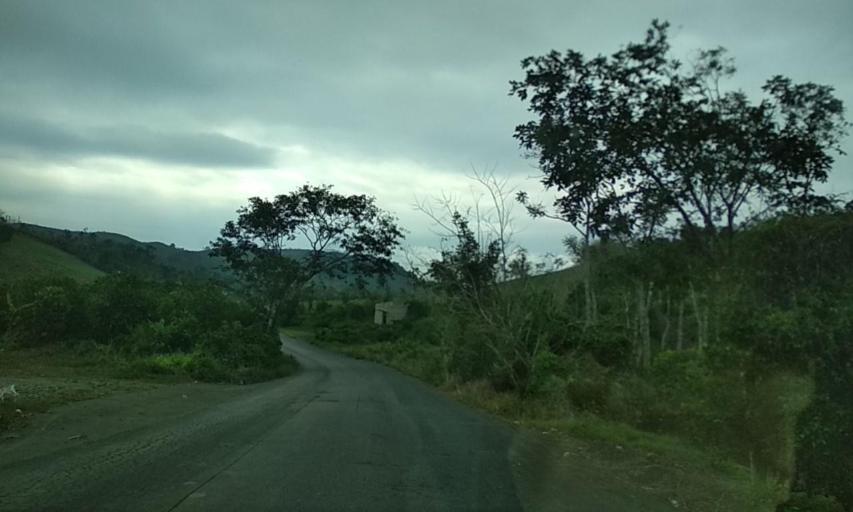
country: MX
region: Veracruz
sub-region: Coatzintla
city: Manuel Maria Contreras
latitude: 20.3661
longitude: -97.5141
